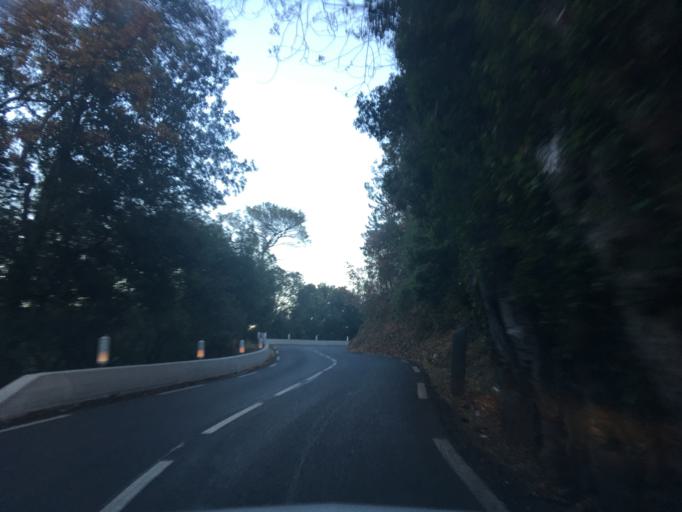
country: FR
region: Provence-Alpes-Cote d'Azur
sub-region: Departement des Alpes-Maritimes
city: Le Tignet
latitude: 43.6247
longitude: 6.8211
